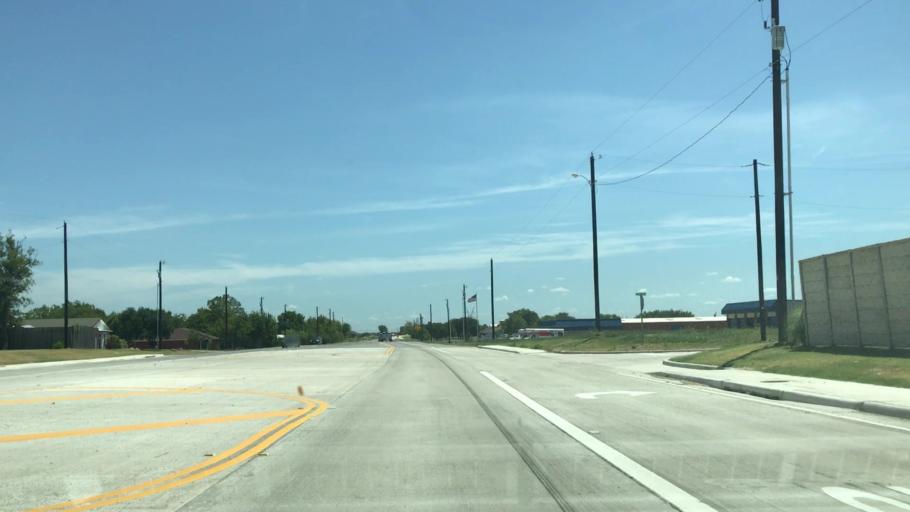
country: US
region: Texas
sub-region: Collin County
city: Saint Paul
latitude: 33.0514
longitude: -96.5611
